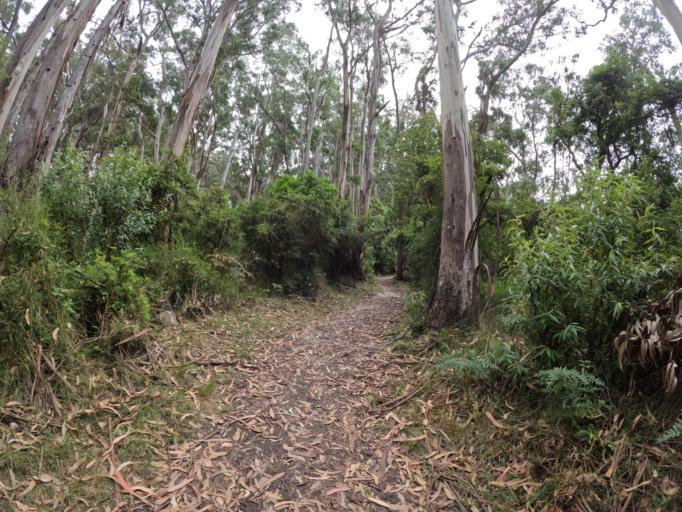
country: AU
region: Victoria
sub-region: Colac-Otway
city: Apollo Bay
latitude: -38.7926
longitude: 143.6167
